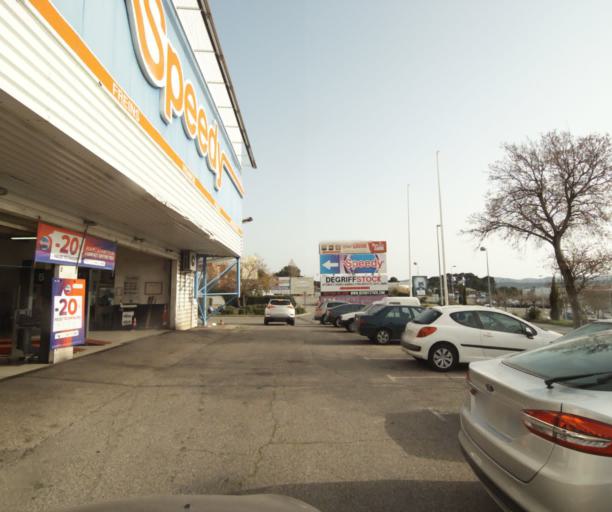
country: FR
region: Provence-Alpes-Cote d'Azur
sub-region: Departement des Bouches-du-Rhone
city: Vitrolles
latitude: 43.4336
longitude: 5.2623
